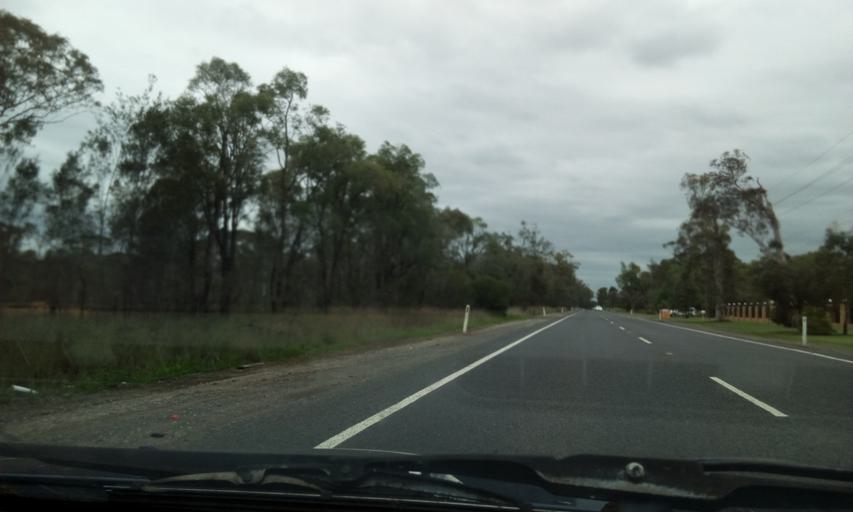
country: AU
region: New South Wales
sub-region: Penrith Municipality
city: Werrington Downs
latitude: -33.6732
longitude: 150.7499
